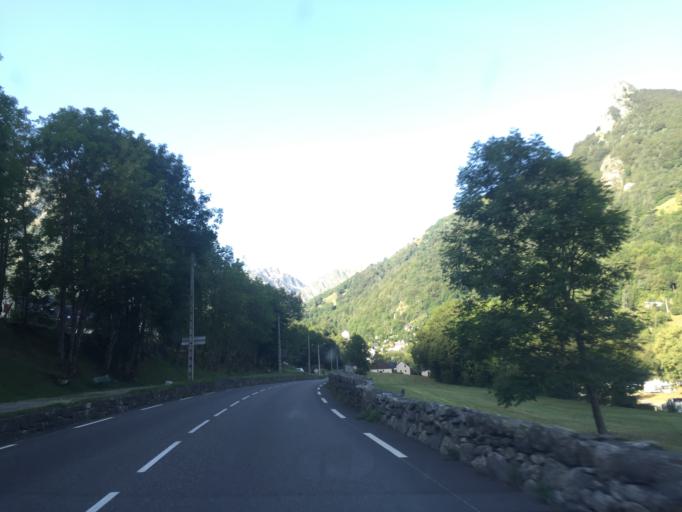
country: FR
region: Midi-Pyrenees
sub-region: Departement des Hautes-Pyrenees
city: Cauterets
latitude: 42.9006
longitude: -0.1070
